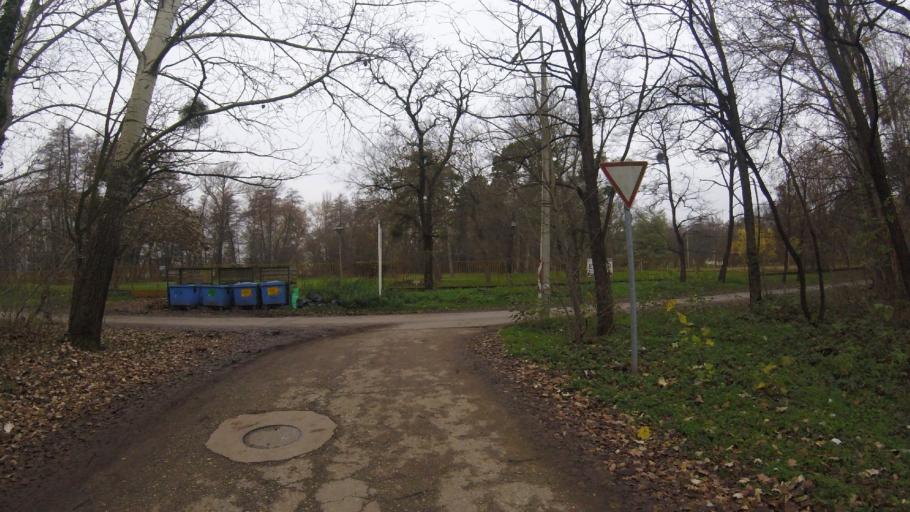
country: HU
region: Komarom-Esztergom
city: Baj
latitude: 47.6352
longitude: 18.3419
